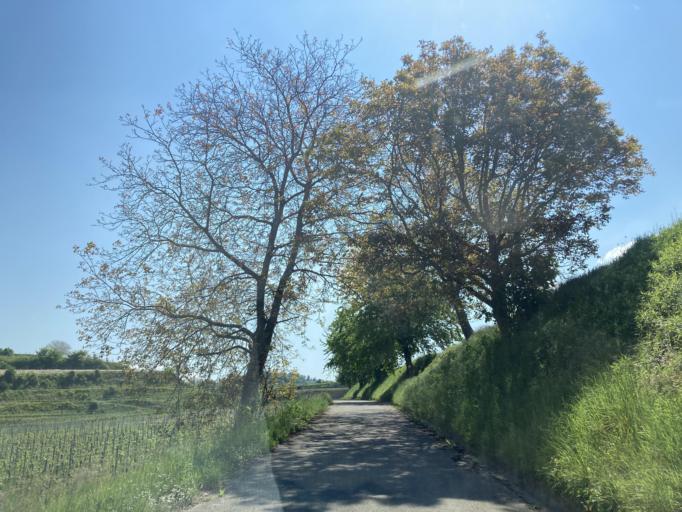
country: DE
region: Baden-Wuerttemberg
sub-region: Freiburg Region
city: Vogtsburg
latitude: 48.0776
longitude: 7.6155
